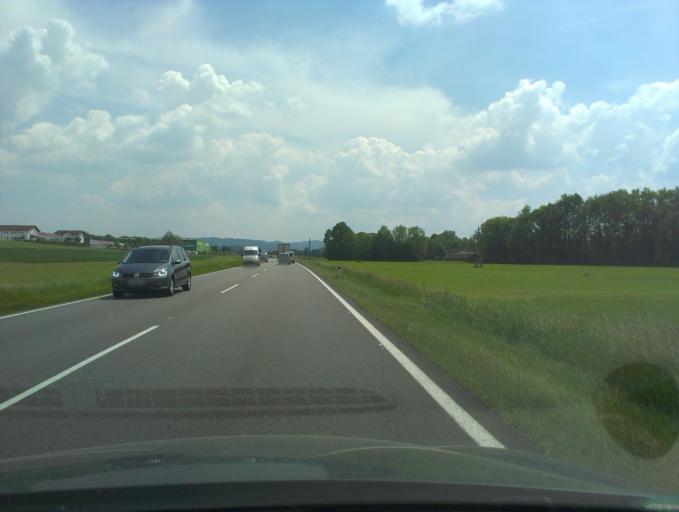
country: AT
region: Upper Austria
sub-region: Politischer Bezirk Ried im Innkreis
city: Ried im Innkreis
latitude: 48.2057
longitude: 13.5301
